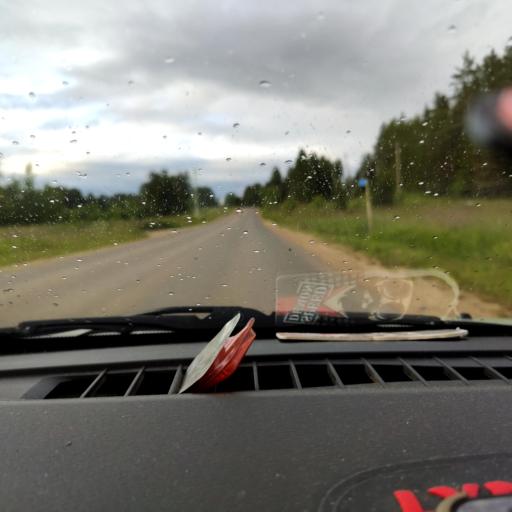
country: RU
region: Perm
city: Ocher
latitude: 57.9146
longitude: 54.7597
